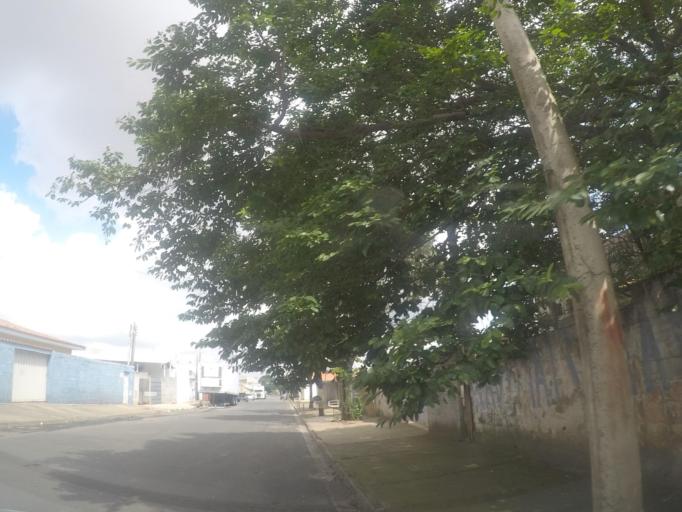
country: BR
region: Sao Paulo
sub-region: Hortolandia
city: Hortolandia
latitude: -22.8560
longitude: -47.1620
